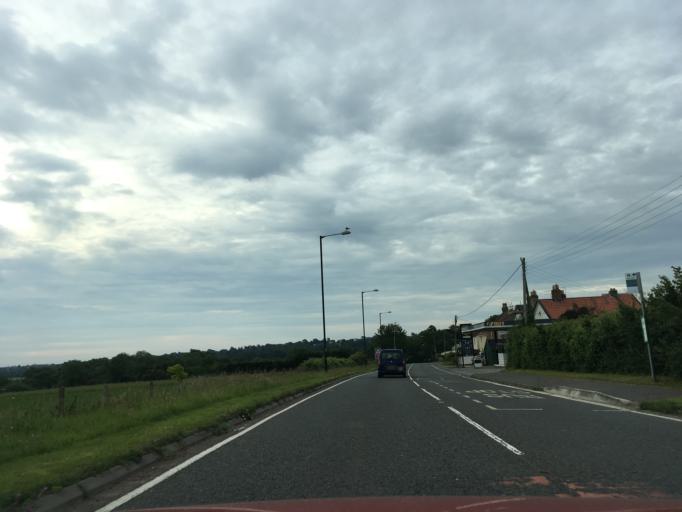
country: GB
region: England
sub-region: North Somerset
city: Easton-in-Gordano
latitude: 51.4702
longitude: -2.6833
